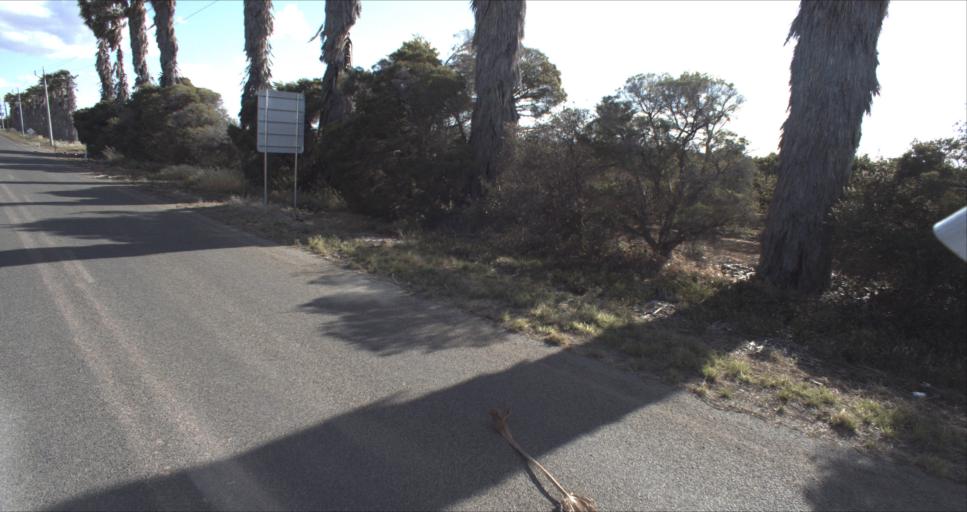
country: AU
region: New South Wales
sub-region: Leeton
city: Leeton
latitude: -34.5224
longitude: 146.2830
